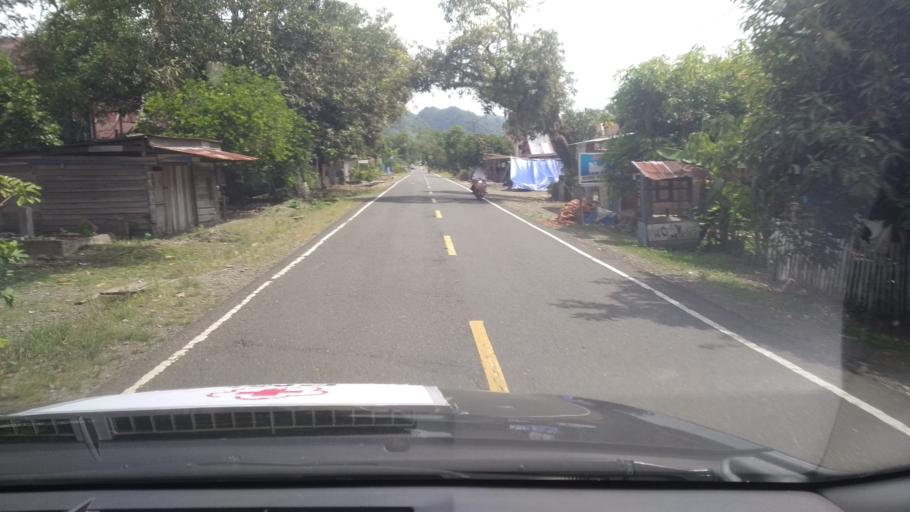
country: ID
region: Sulawesi Barat
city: Tapalang
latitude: -2.8843
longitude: 118.8853
